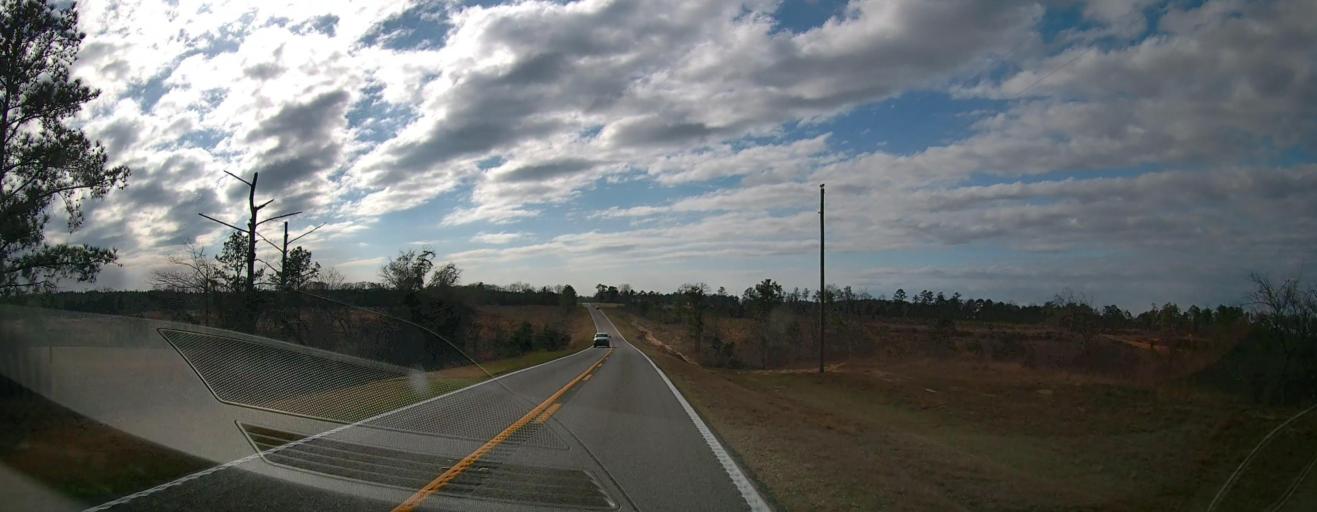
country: US
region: Georgia
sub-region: Marion County
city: Buena Vista
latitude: 32.4447
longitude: -84.5259
